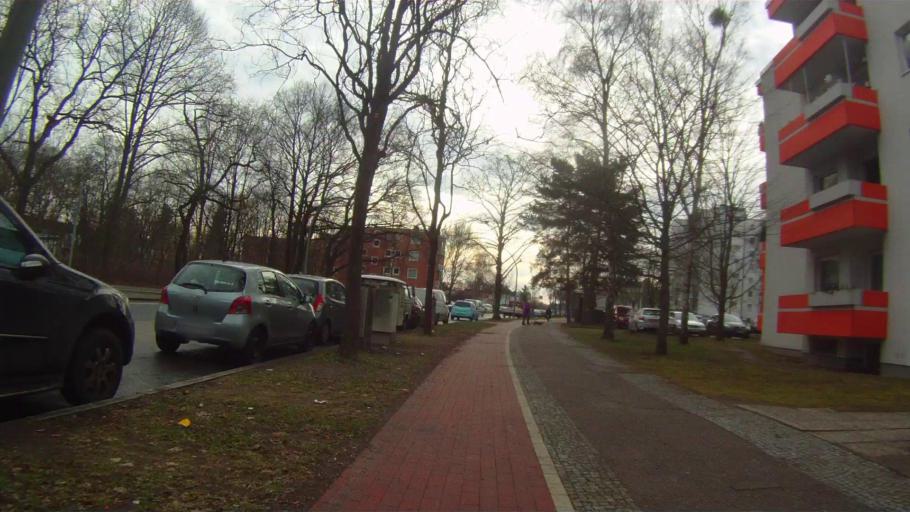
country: DE
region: Berlin
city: Lichtenrade
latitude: 52.4235
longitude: 13.4146
